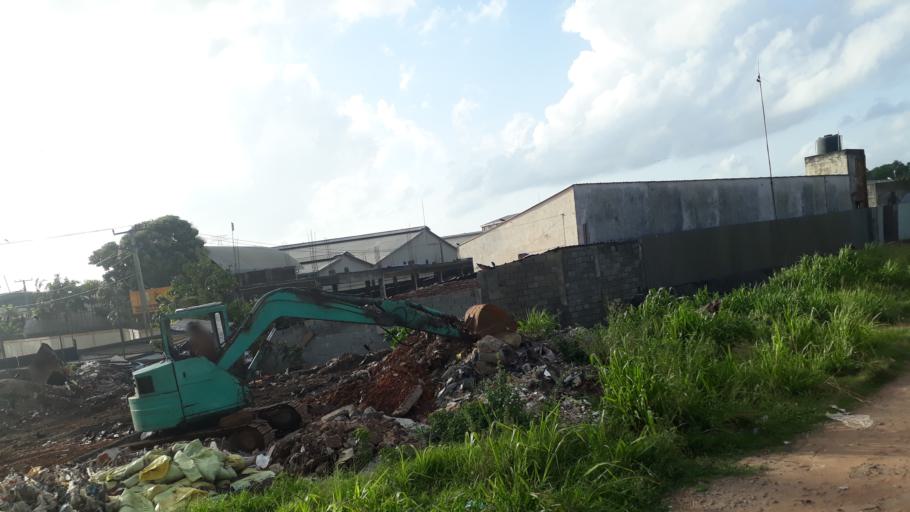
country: LK
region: Western
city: Kolonnawa
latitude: 6.9446
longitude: 79.8850
